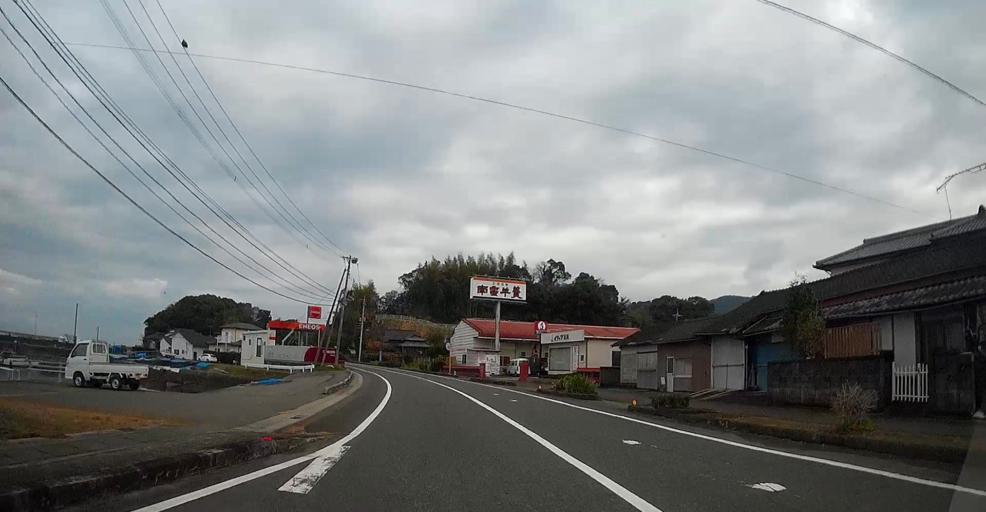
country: JP
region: Kumamoto
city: Hondo
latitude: 32.4611
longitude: 130.2355
